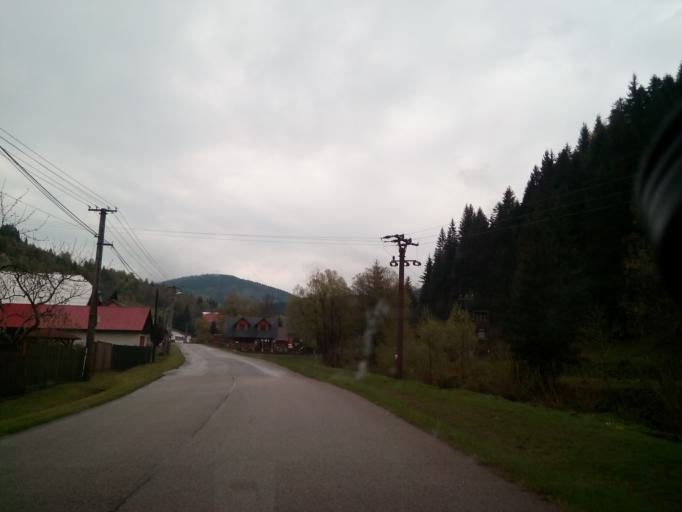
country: SK
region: Zilinsky
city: Oravska Lesna
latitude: 49.2970
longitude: 19.1832
